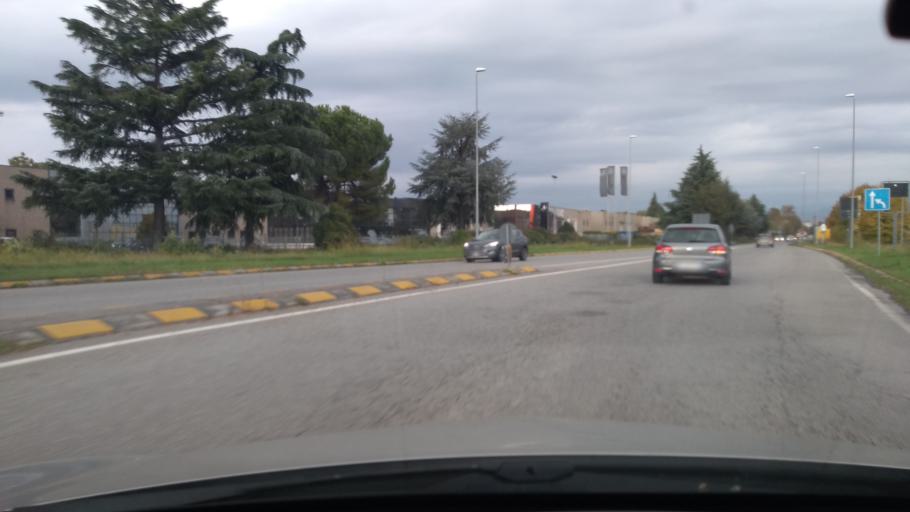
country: IT
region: Lombardy
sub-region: Provincia di Bergamo
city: Arcene
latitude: 45.5908
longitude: 9.6206
